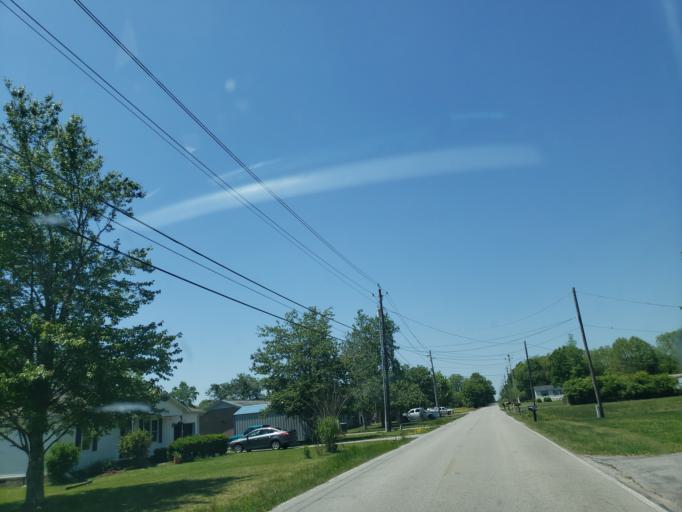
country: US
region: Alabama
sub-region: Madison County
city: Harvest
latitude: 34.9623
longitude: -86.6936
